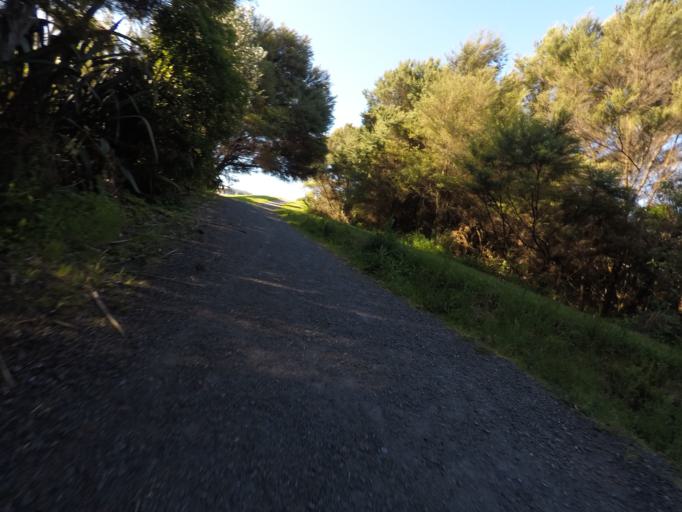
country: NZ
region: Auckland
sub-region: Auckland
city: Rosebank
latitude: -36.8487
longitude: 174.6539
